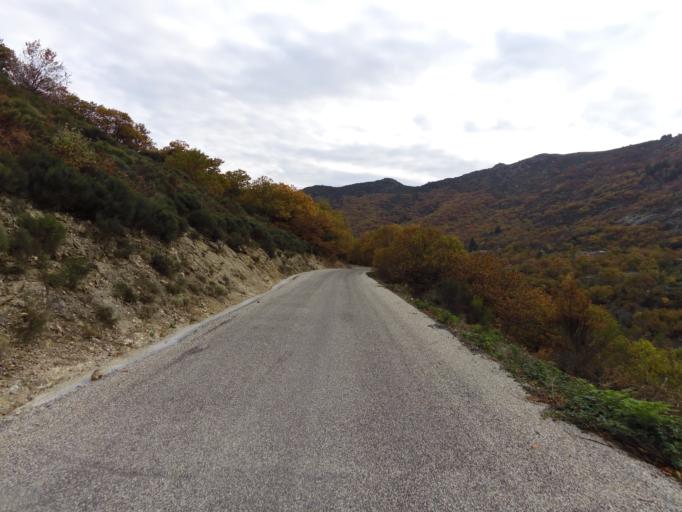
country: FR
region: Rhone-Alpes
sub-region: Departement de l'Ardeche
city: Les Vans
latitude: 44.4998
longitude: 4.0381
